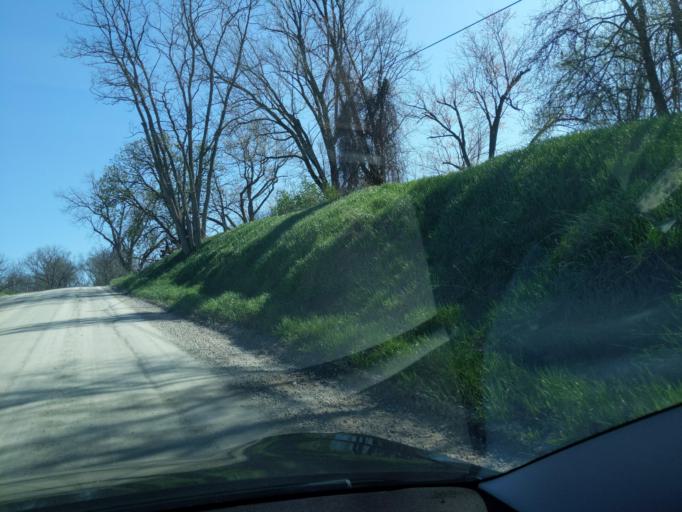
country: US
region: Michigan
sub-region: Washtenaw County
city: Chelsea
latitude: 42.3939
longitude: -84.0837
